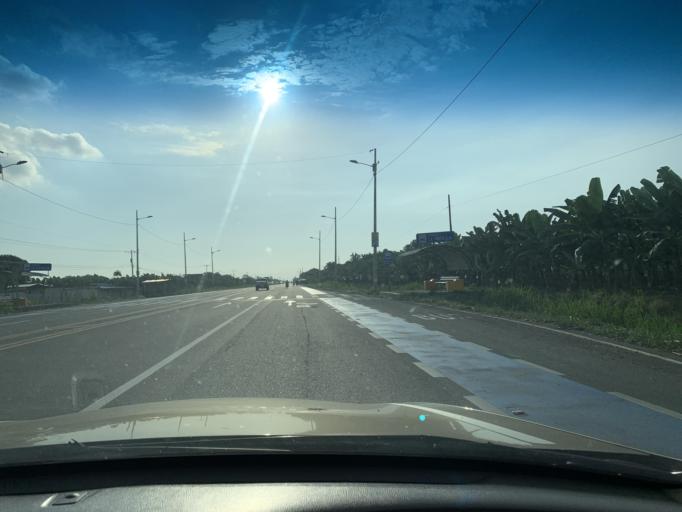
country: EC
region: Guayas
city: Naranjito
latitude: -2.2572
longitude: -79.5787
